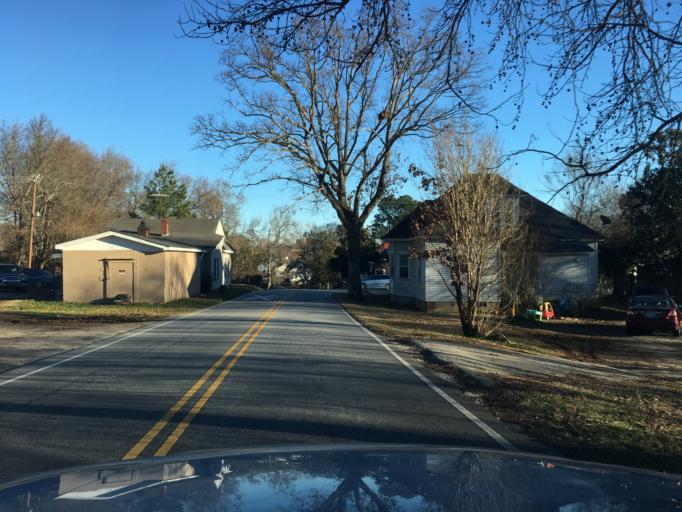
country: US
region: South Carolina
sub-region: Greenville County
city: Greer
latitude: 34.9378
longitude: -82.2430
